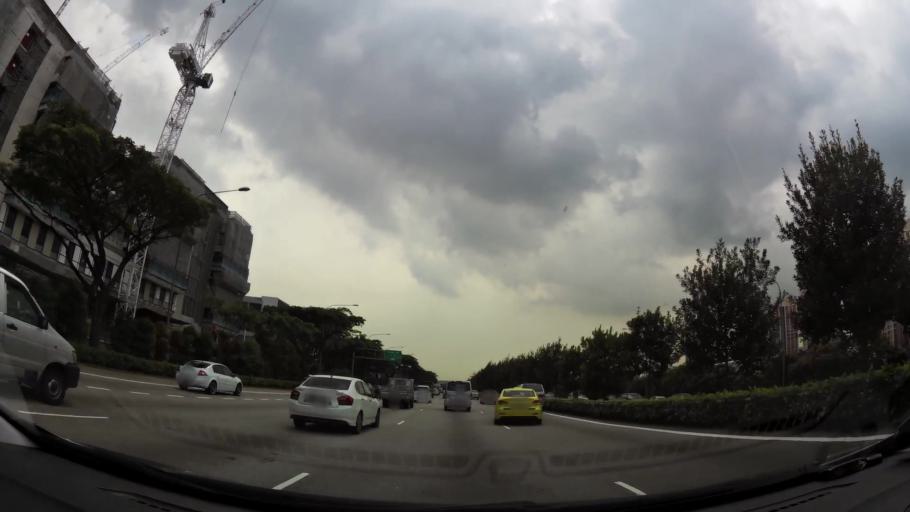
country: SG
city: Singapore
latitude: 1.3506
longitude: 103.8579
